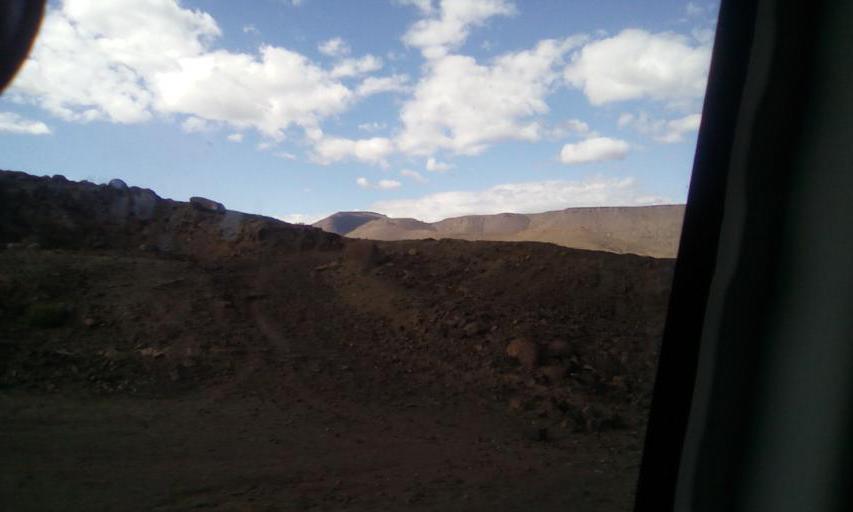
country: LS
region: Qacha's Nek
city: Qacha's Nek
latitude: -30.0228
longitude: 28.1845
